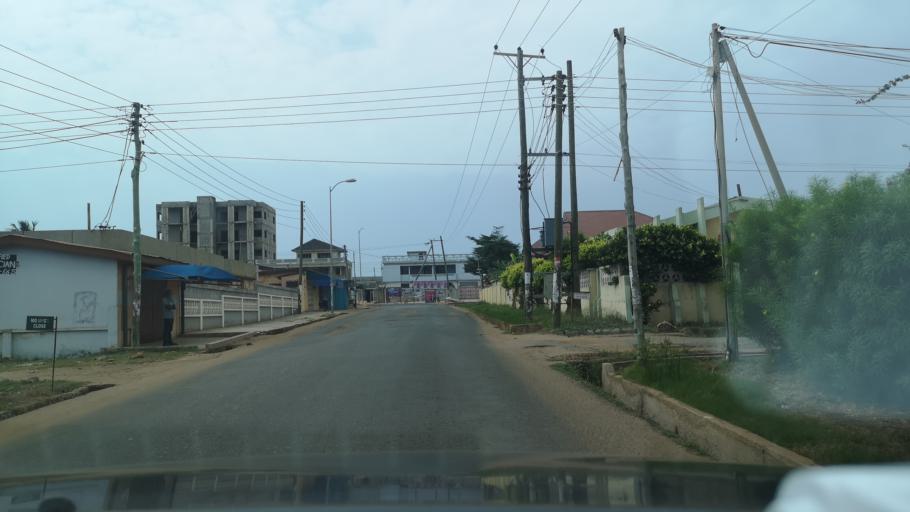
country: GH
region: Greater Accra
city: Nungua
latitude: 5.6150
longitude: -0.0513
